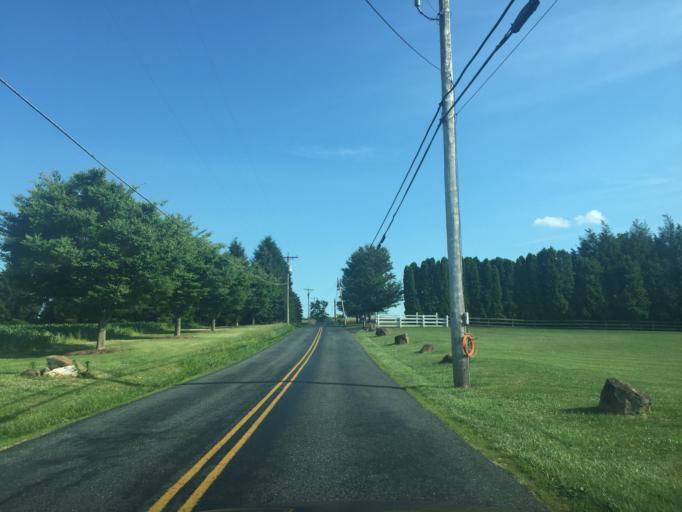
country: US
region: Maryland
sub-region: Harford County
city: Jarrettsville
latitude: 39.6512
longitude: -76.4735
